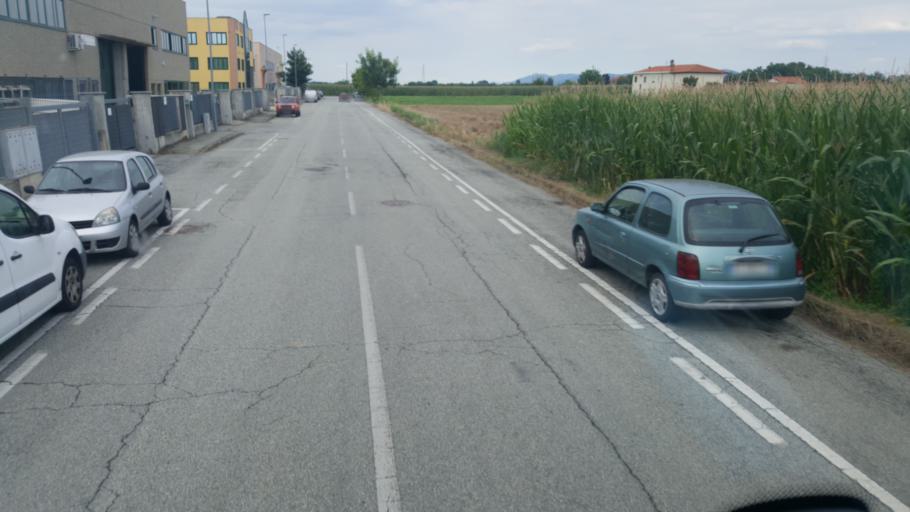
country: IT
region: Piedmont
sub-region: Provincia di Torino
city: Gerbole-Zucche
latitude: 44.9839
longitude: 7.5306
